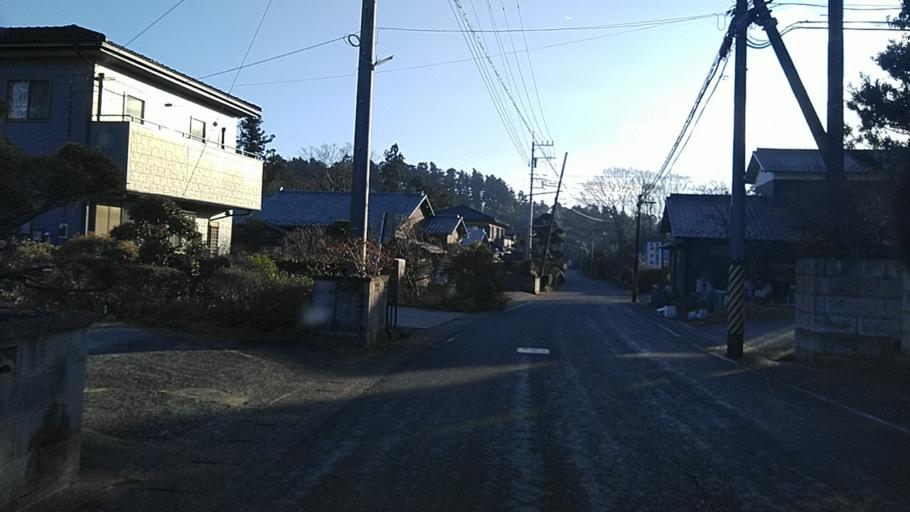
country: JP
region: Chiba
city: Kimitsu
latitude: 35.2549
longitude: 139.9598
